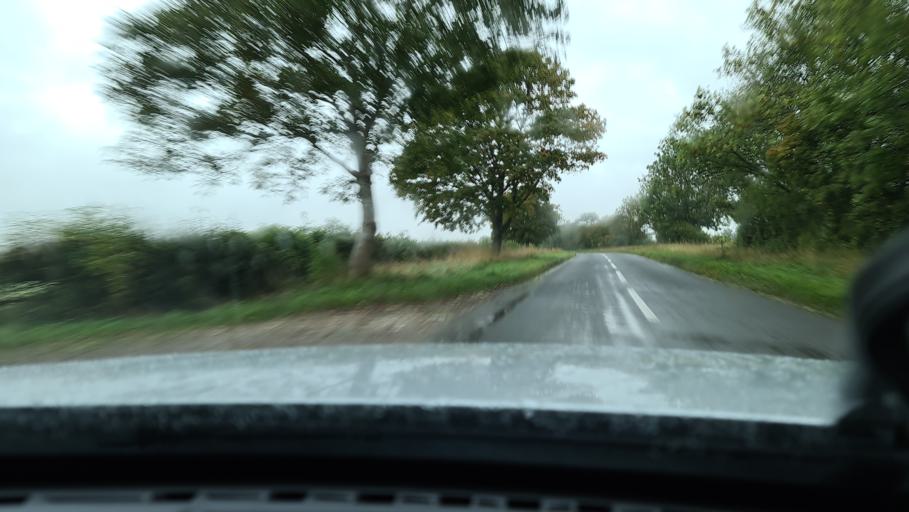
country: GB
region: England
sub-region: Oxfordshire
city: Woodstock
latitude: 51.8827
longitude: -1.3685
